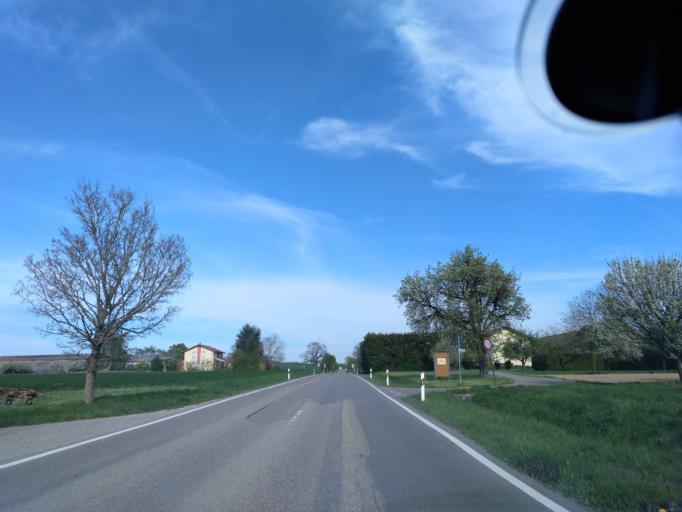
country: DE
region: Baden-Wuerttemberg
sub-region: Regierungsbezirk Stuttgart
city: Kupferzell
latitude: 49.2329
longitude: 9.7184
